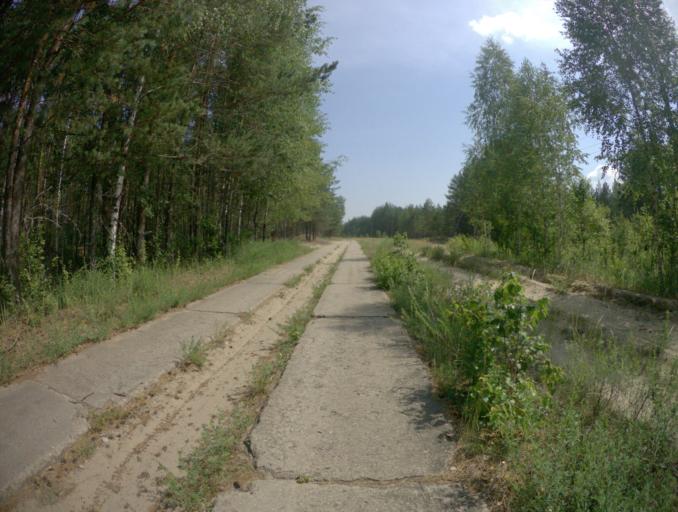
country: RU
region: Ivanovo
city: Talitsy
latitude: 56.4015
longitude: 42.4191
